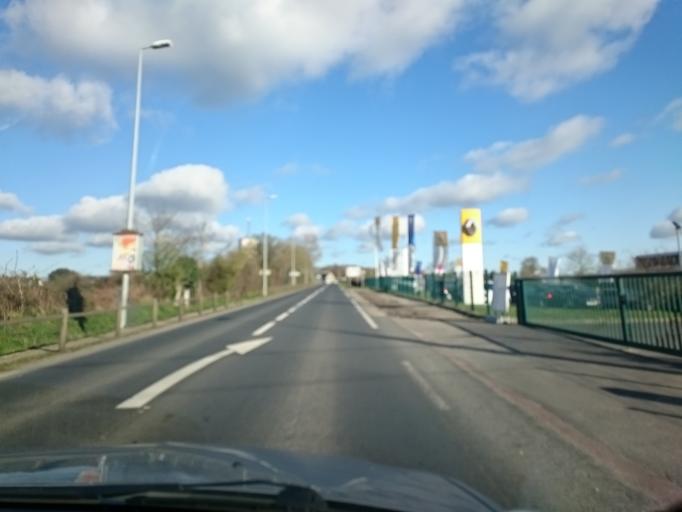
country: FR
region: Lower Normandy
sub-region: Departement de la Manche
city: Valognes
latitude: 49.5018
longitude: -1.4571
